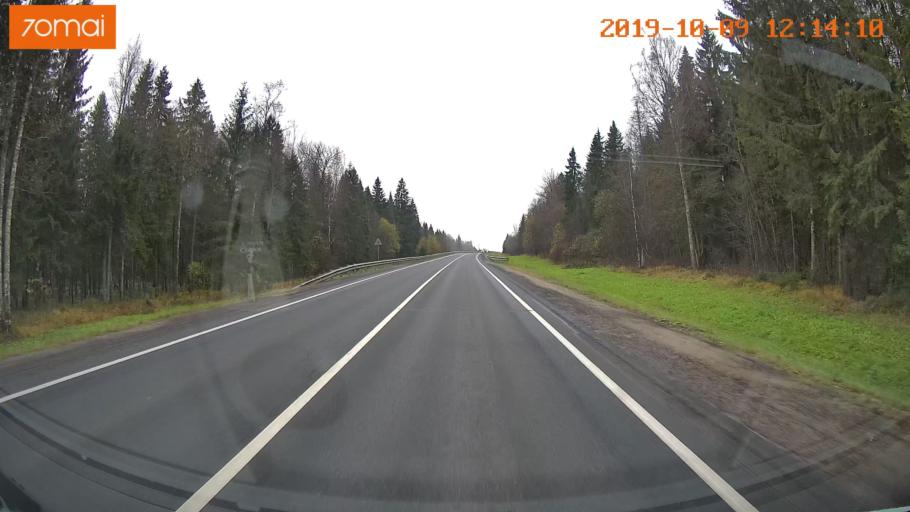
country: RU
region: Jaroslavl
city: Prechistoye
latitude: 58.4996
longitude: 40.3401
